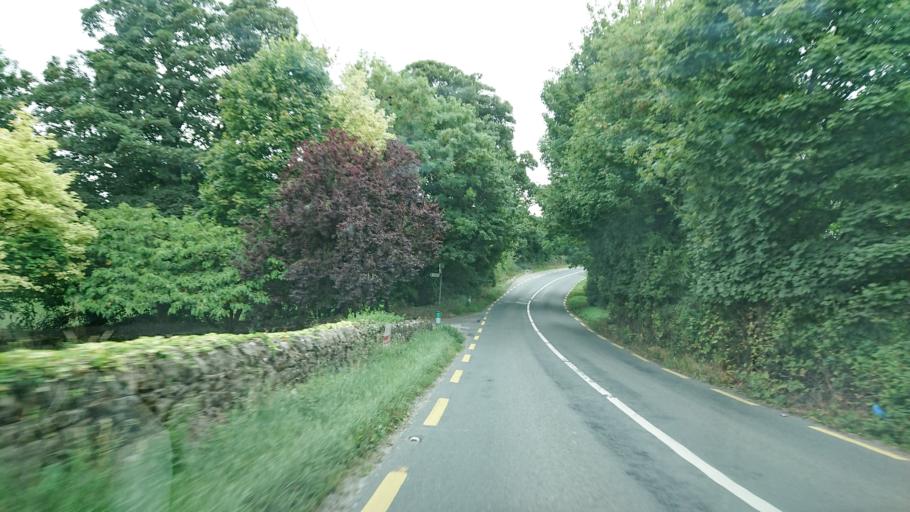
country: IE
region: Munster
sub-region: County Cork
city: Mallow
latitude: 52.1502
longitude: -8.6045
